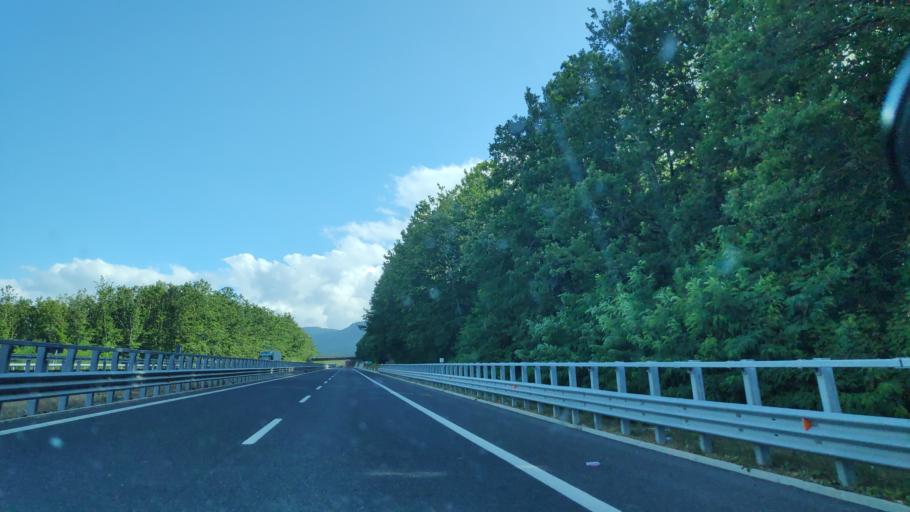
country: IT
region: Campania
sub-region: Provincia di Salerno
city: Buonabitacolo
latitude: 40.2501
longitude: 15.6603
